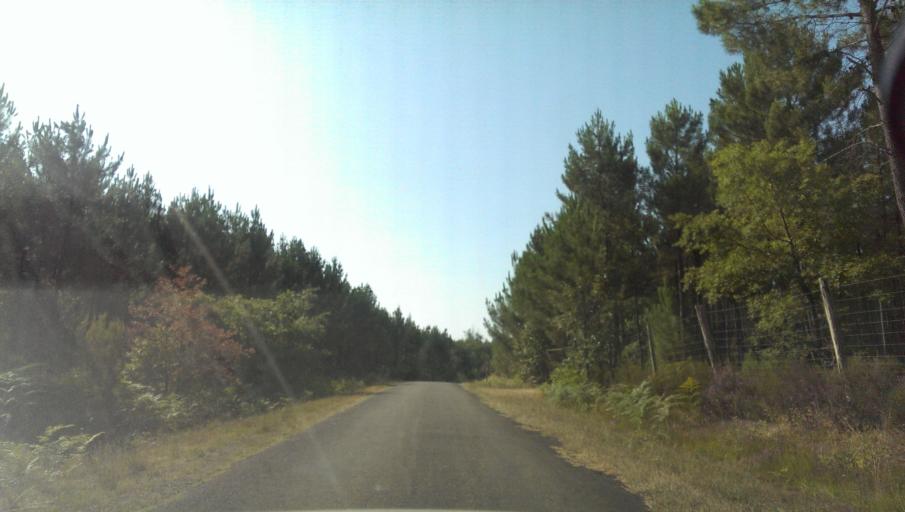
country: FR
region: Aquitaine
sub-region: Departement des Landes
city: Sarbazan
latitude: 44.0847
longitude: -0.1566
